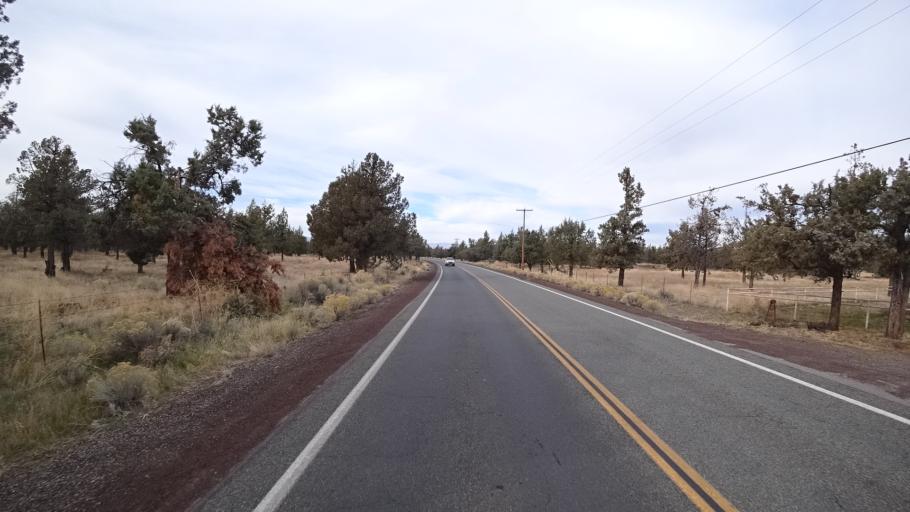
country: US
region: California
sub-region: Siskiyou County
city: Weed
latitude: 41.5914
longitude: -122.3059
